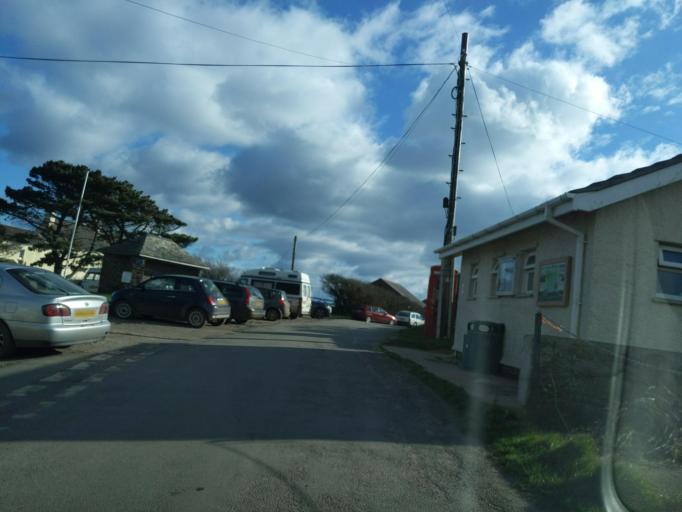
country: GB
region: England
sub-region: Devon
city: Salcombe
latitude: 50.2148
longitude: -3.7101
